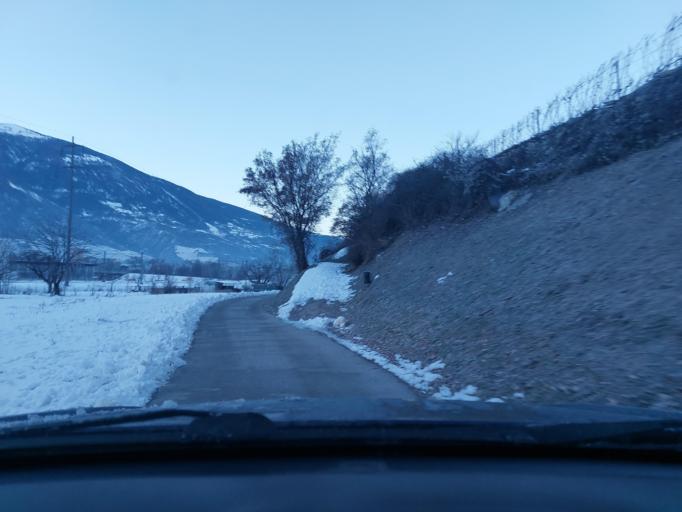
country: CH
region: Valais
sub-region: Sierre District
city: Chalais
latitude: 46.2829
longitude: 7.5163
